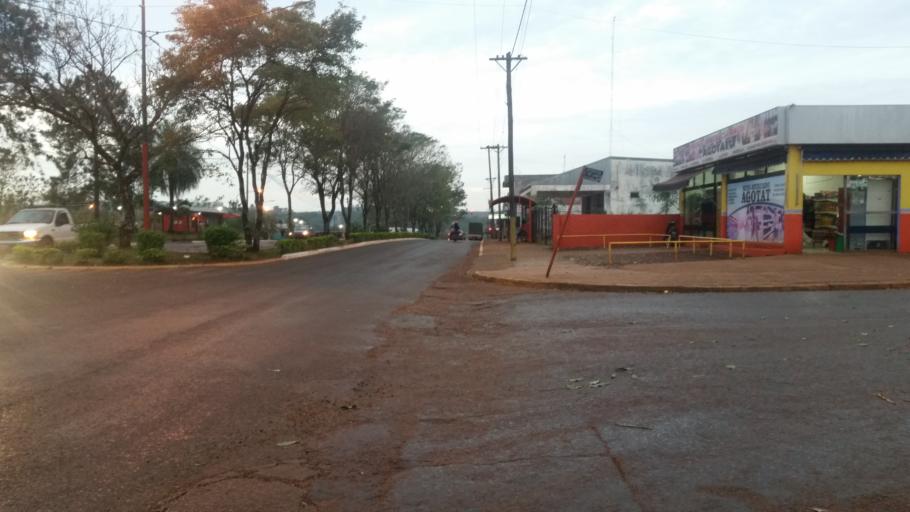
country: AR
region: Misiones
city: Puerto Esperanza
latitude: -26.0226
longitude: -54.6060
